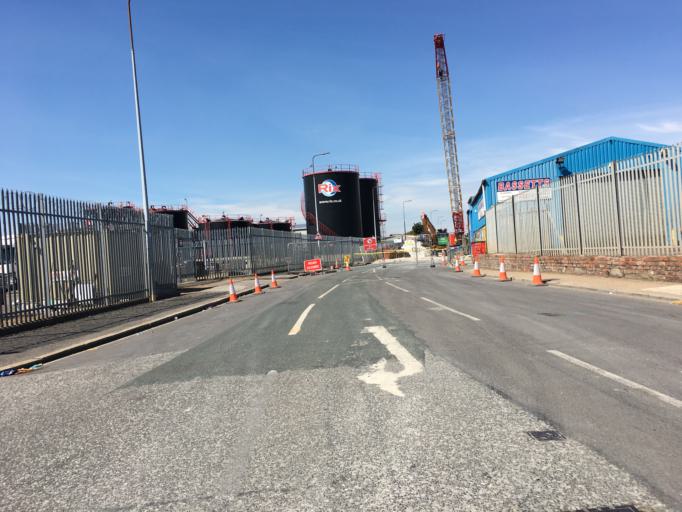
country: GB
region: England
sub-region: City of Kingston upon Hull
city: Hull
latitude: 53.7571
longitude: -0.3347
